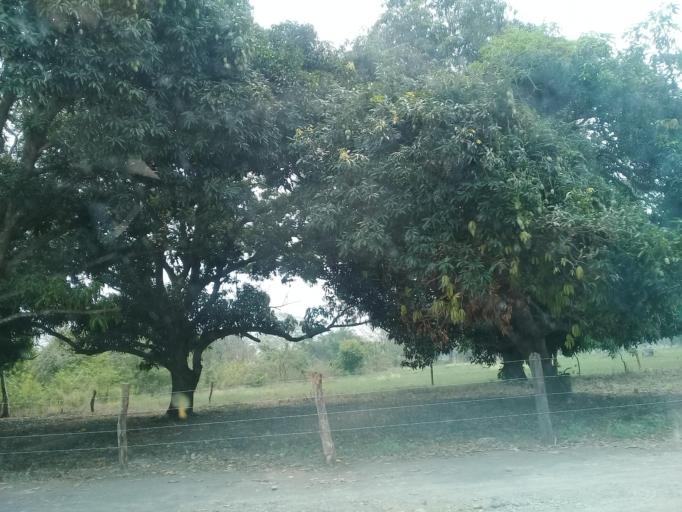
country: MX
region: Veracruz
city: Jamapa
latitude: 18.9535
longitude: -96.2060
